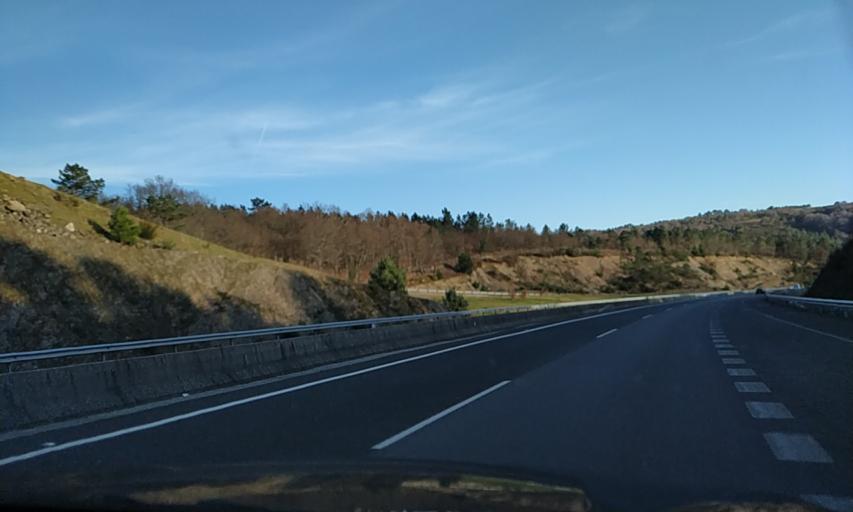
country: ES
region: Galicia
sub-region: Provincia de Pontevedra
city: Lalin
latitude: 42.6205
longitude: -8.0989
